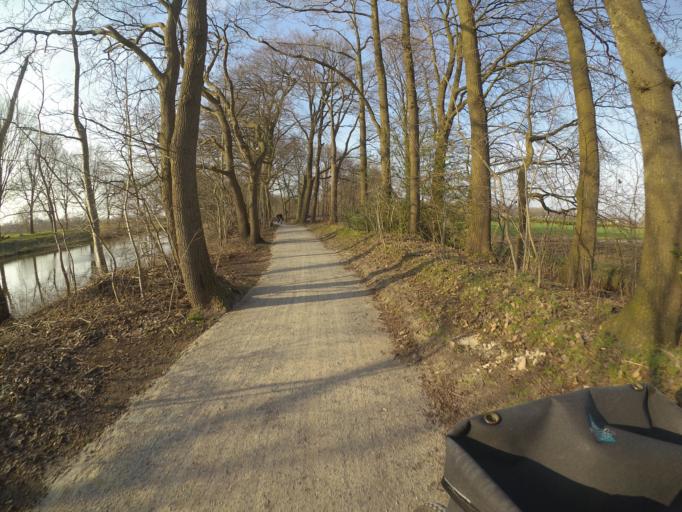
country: NL
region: North Brabant
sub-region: Gemeente Dongen
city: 's Gravenmoer
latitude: 51.6527
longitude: 4.9329
